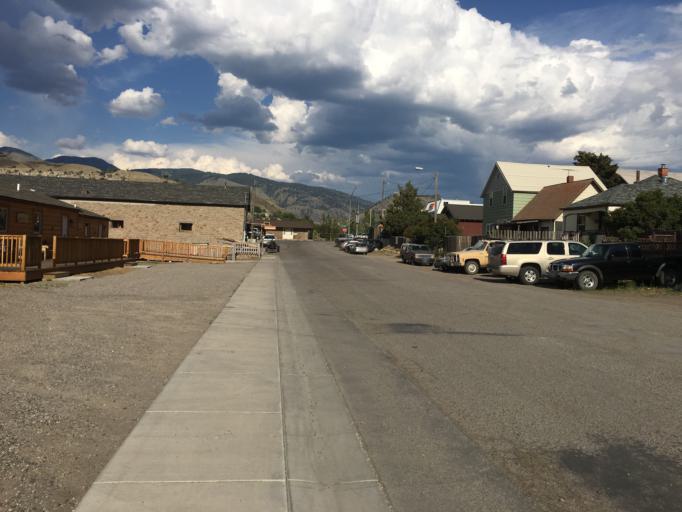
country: US
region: Montana
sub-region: Gallatin County
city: West Yellowstone
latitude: 45.0313
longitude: -110.7071
